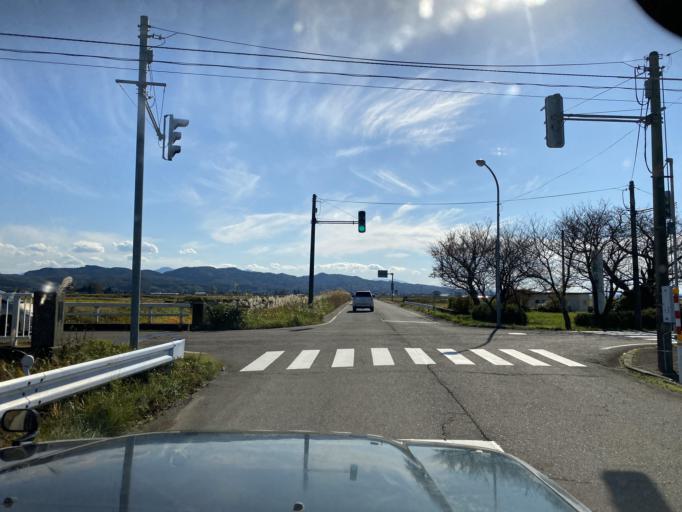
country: JP
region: Niigata
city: Niitsu-honcho
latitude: 37.7733
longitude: 139.0832
